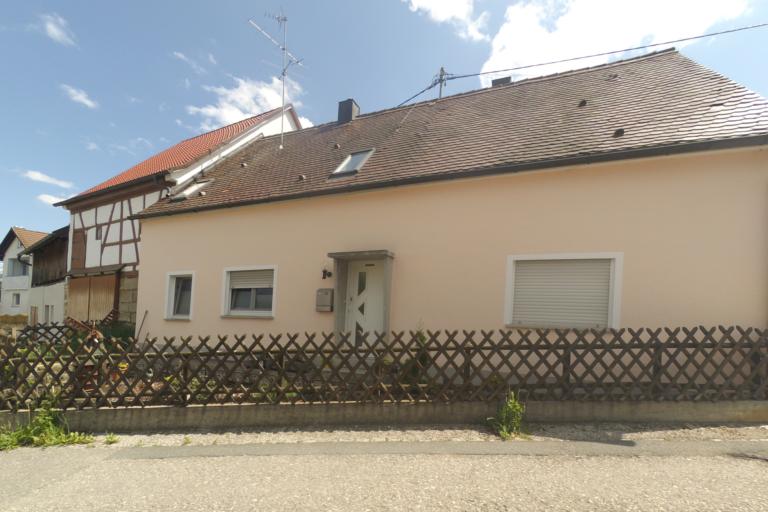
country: DE
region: Bavaria
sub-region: Upper Franconia
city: Hallerndorf
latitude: 49.7715
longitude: 10.9483
